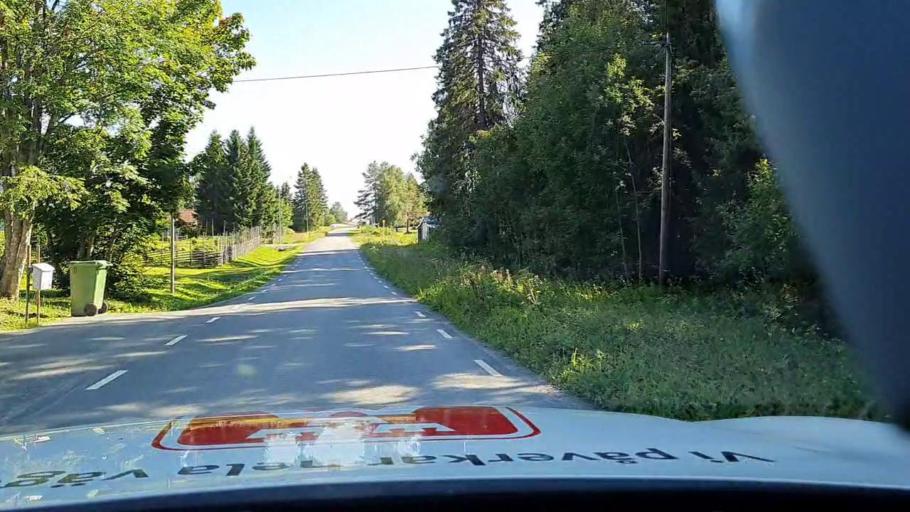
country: SE
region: Jaemtland
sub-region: Krokoms Kommun
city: Krokom
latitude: 63.6807
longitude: 14.6046
